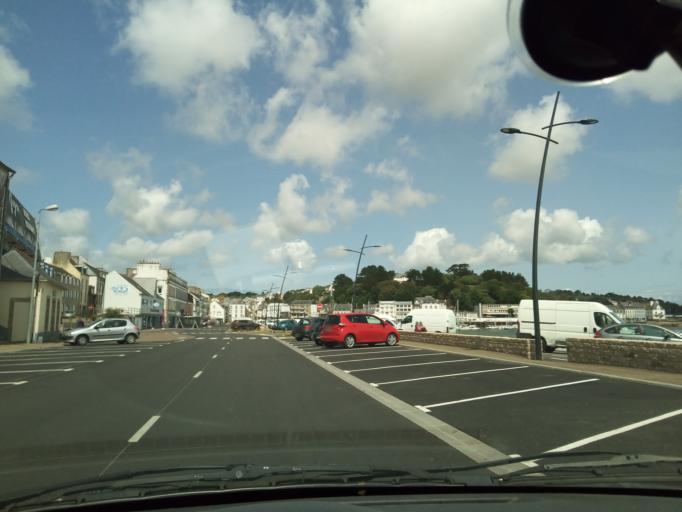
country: FR
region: Brittany
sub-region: Departement du Finistere
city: Audierne
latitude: 48.0204
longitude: -4.5363
